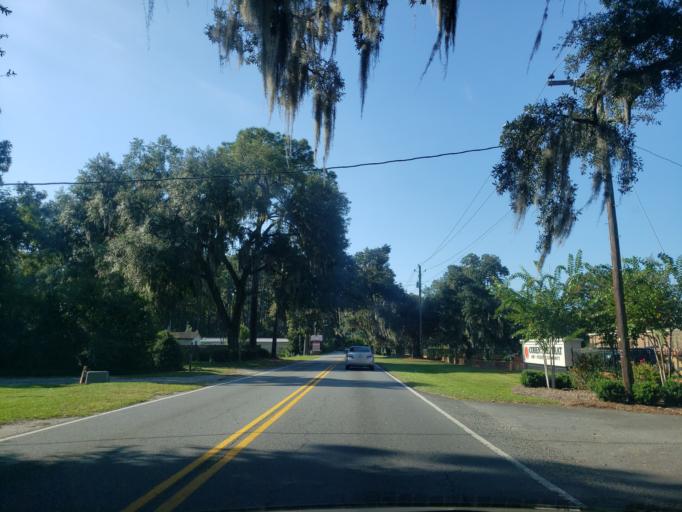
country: US
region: Georgia
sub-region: Chatham County
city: Thunderbolt
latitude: 32.0138
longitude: -81.0778
